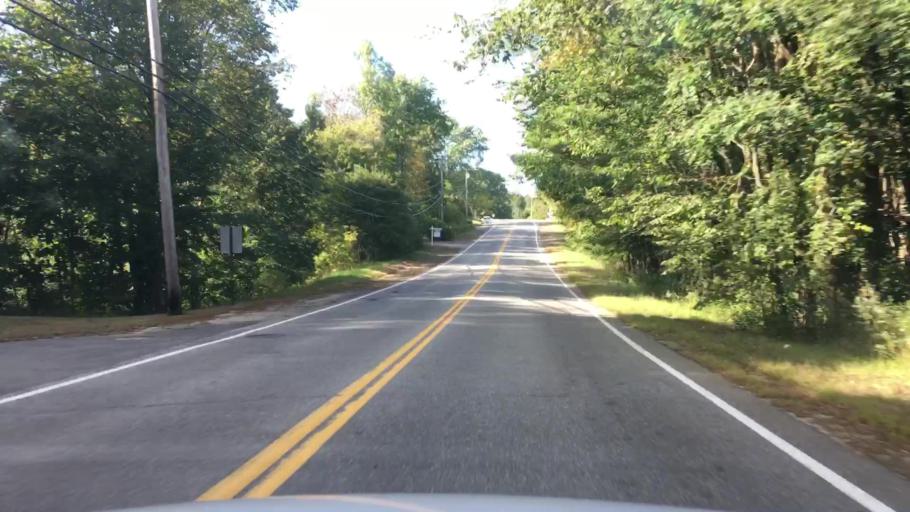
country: US
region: Maine
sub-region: Sagadahoc County
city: Topsham
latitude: 43.9234
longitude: -69.9935
